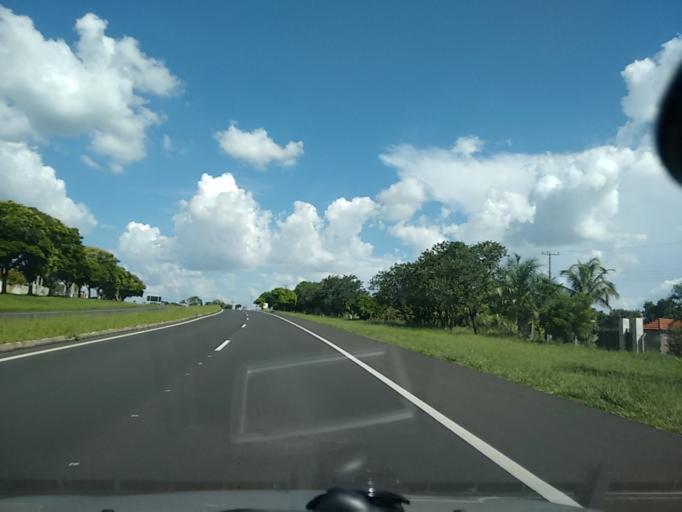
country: BR
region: Sao Paulo
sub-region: Pompeia
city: Pompeia
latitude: -22.1624
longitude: -50.0866
